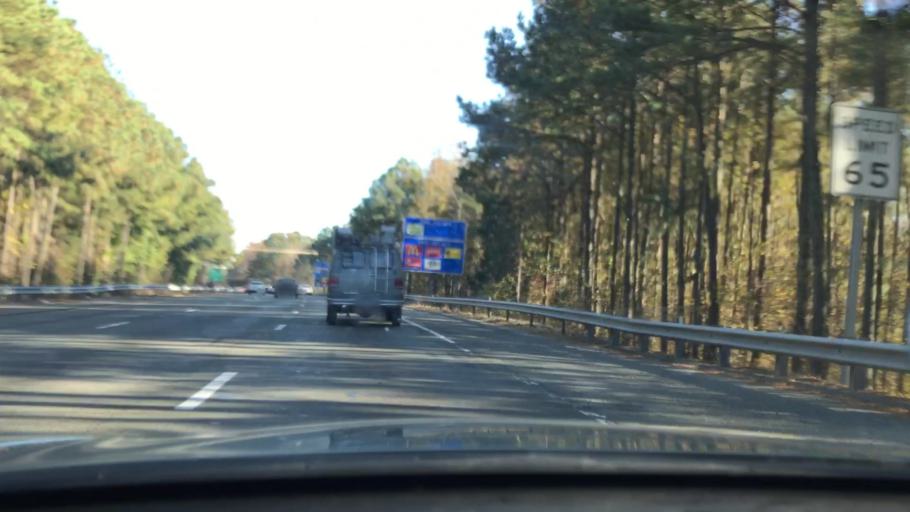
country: US
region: Virginia
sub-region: Henrico County
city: Glen Allen
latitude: 37.6604
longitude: -77.4728
